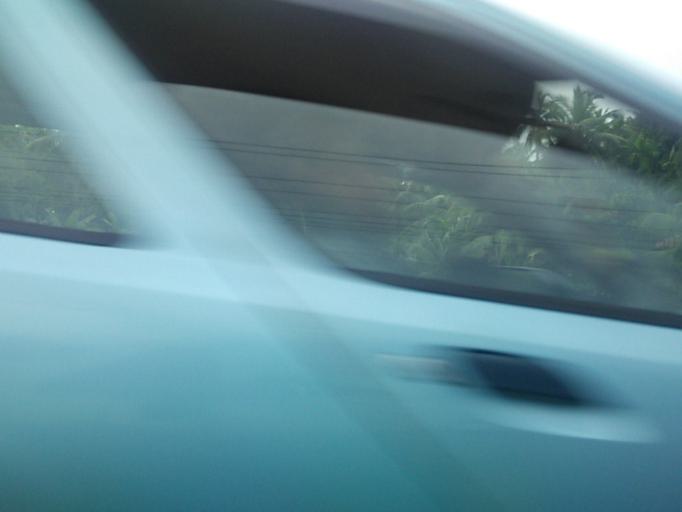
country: IN
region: Kerala
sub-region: Kozhikode
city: Kunnamangalam
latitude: 11.2970
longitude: 75.8355
